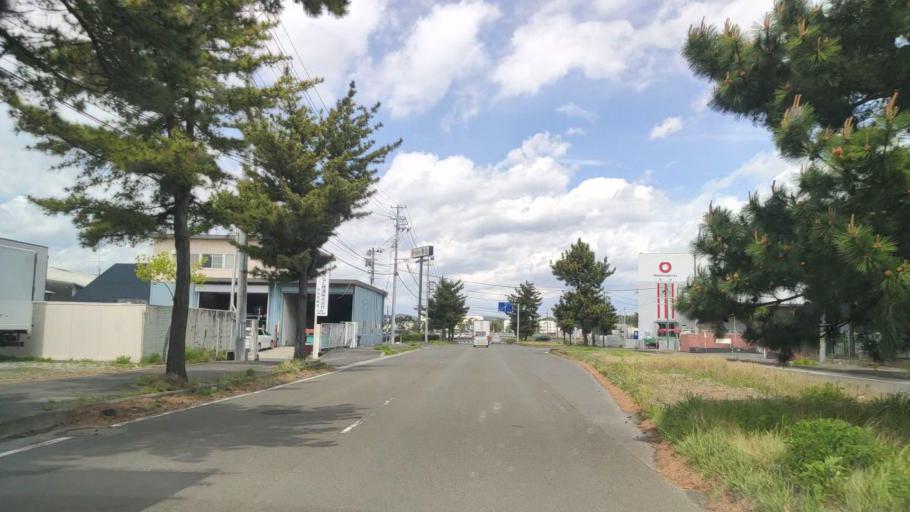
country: JP
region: Miyagi
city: Shiogama
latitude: 38.2877
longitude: 141.0242
